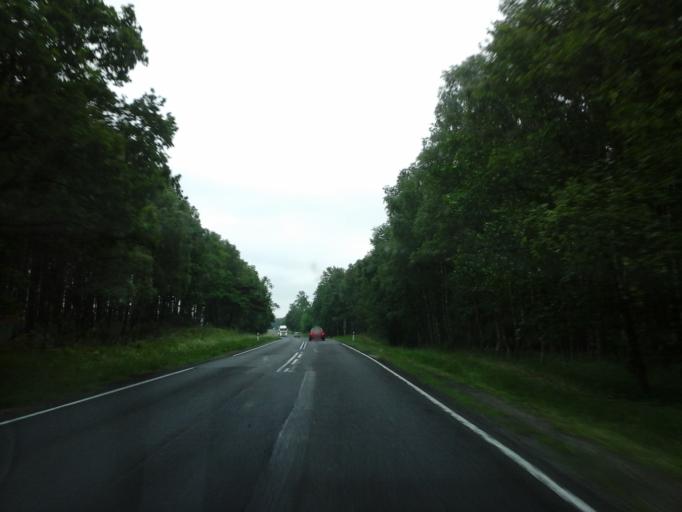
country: PL
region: West Pomeranian Voivodeship
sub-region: Powiat drawski
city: Kalisz Pomorski
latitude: 53.3051
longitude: 15.9821
